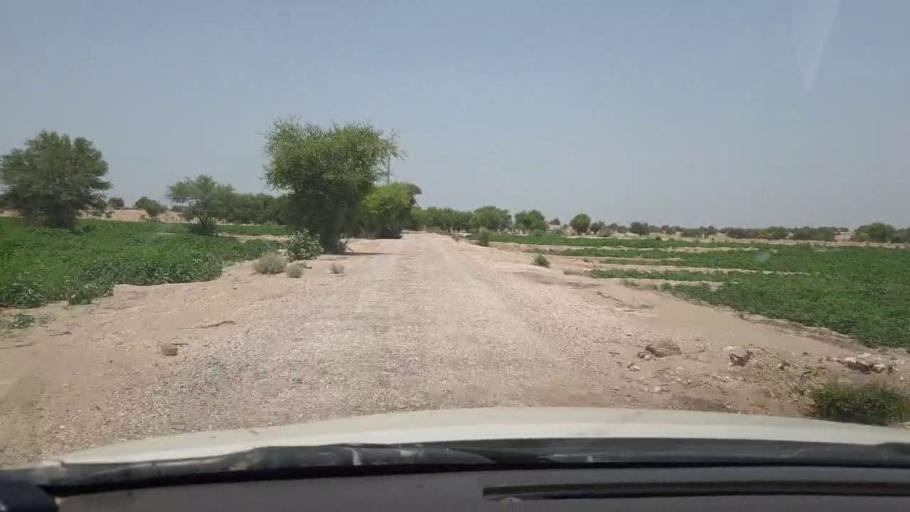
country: PK
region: Sindh
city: Rohri
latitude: 27.5142
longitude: 69.1846
